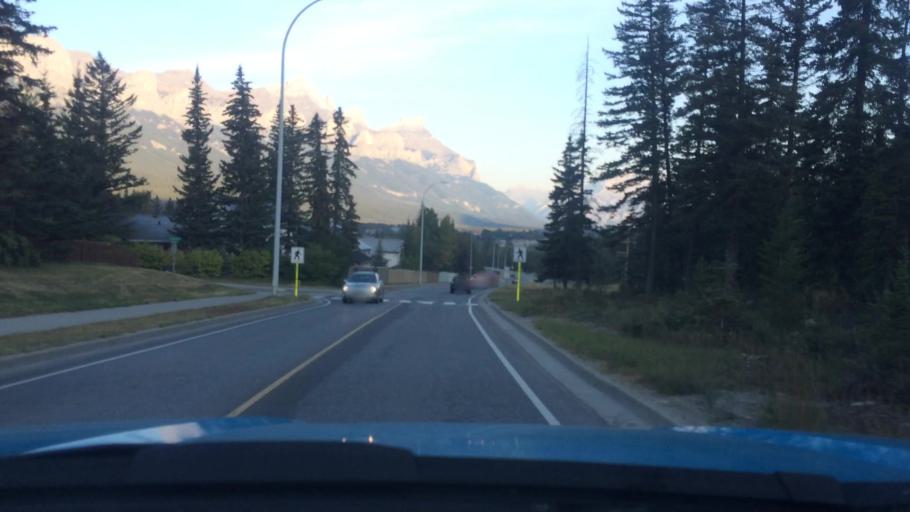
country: CA
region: Alberta
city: Canmore
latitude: 51.0884
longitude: -115.3361
